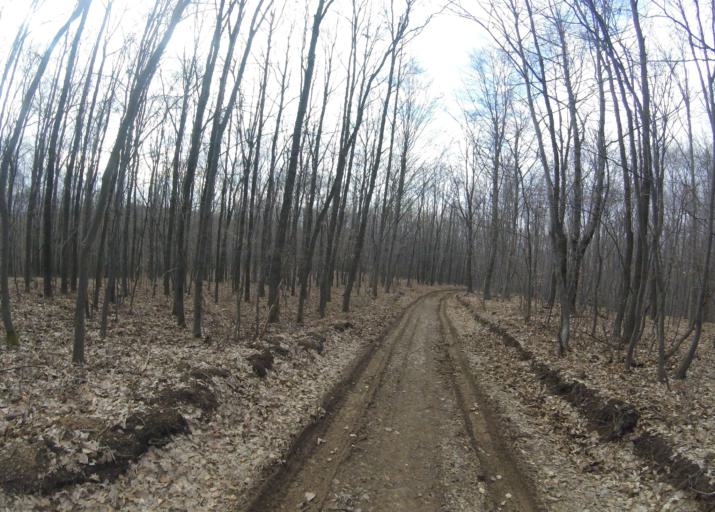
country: HU
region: Heves
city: Belapatfalva
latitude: 48.0283
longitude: 20.3692
